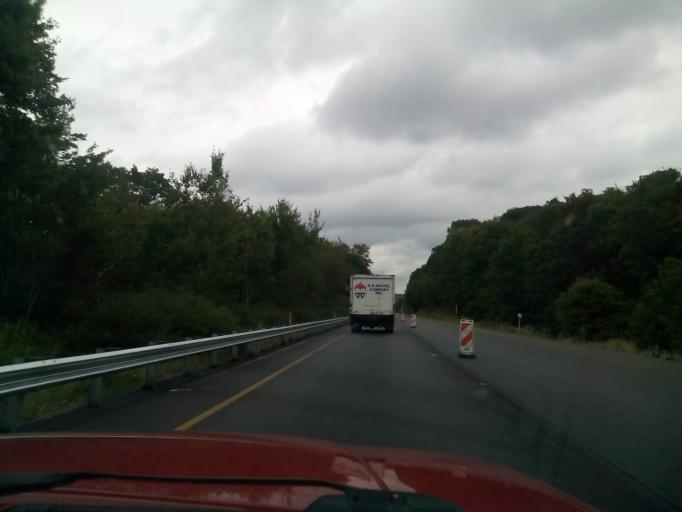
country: US
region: Pennsylvania
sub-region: Jefferson County
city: Falls Creek
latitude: 41.1524
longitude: -78.8428
